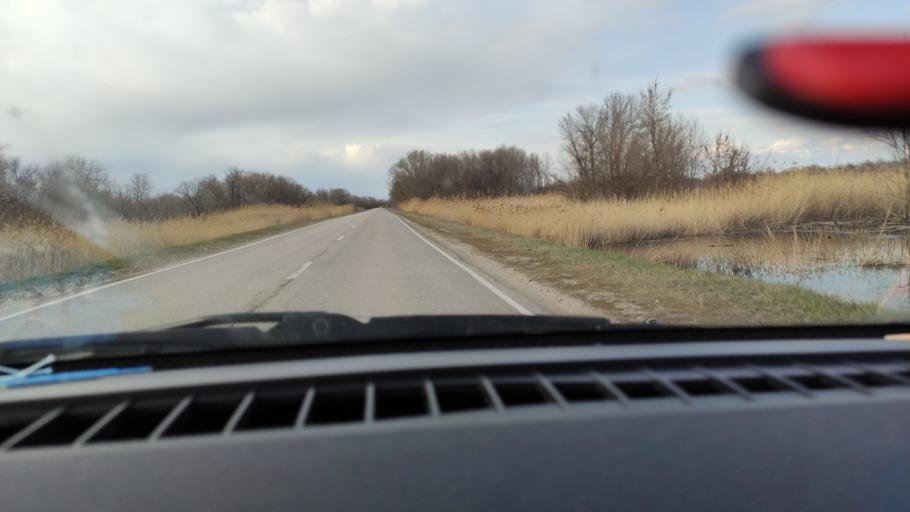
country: RU
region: Saratov
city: Privolzhskiy
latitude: 51.2706
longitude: 45.9471
